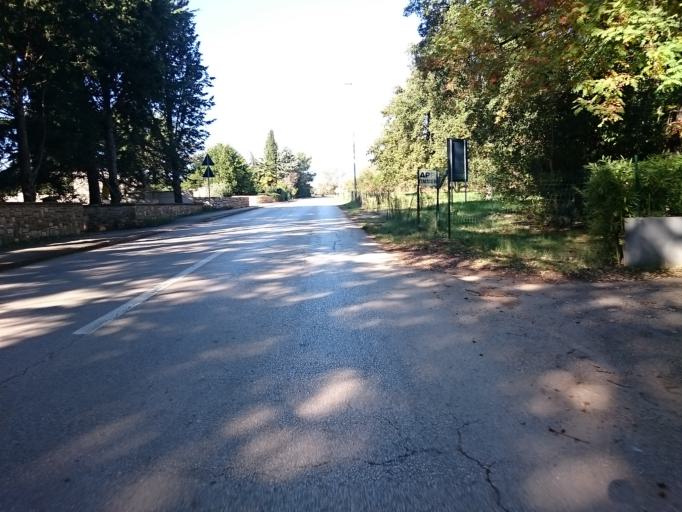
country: HR
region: Istarska
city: Novigrad
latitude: 45.3611
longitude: 13.5514
